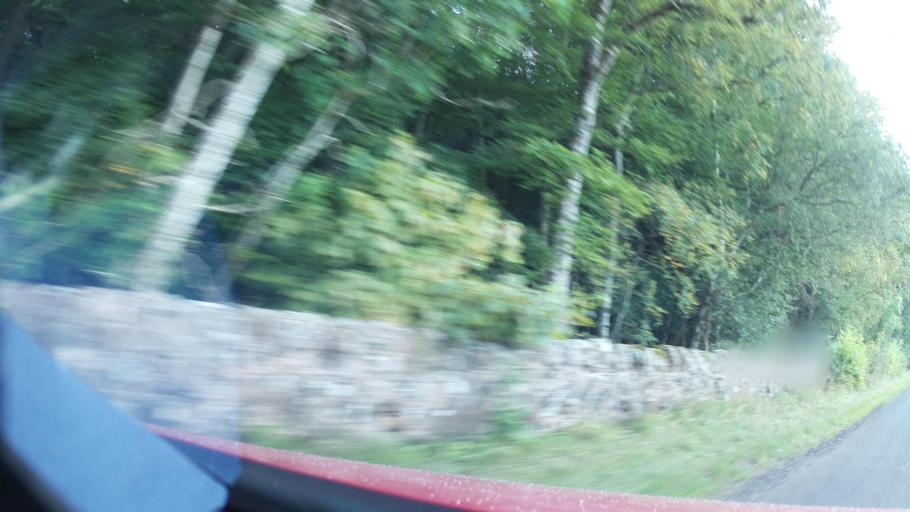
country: GB
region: Scotland
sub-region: Fife
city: Saint Andrews
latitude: 56.2958
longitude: -2.7921
